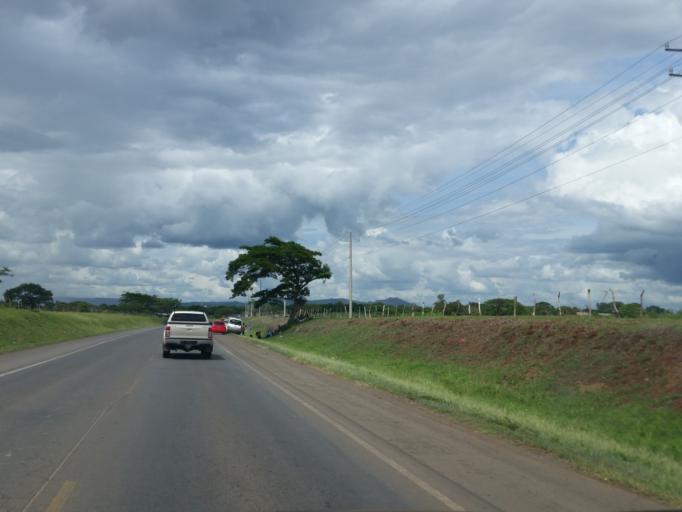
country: NI
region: Managua
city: Tipitapa
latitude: 12.2569
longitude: -86.0847
